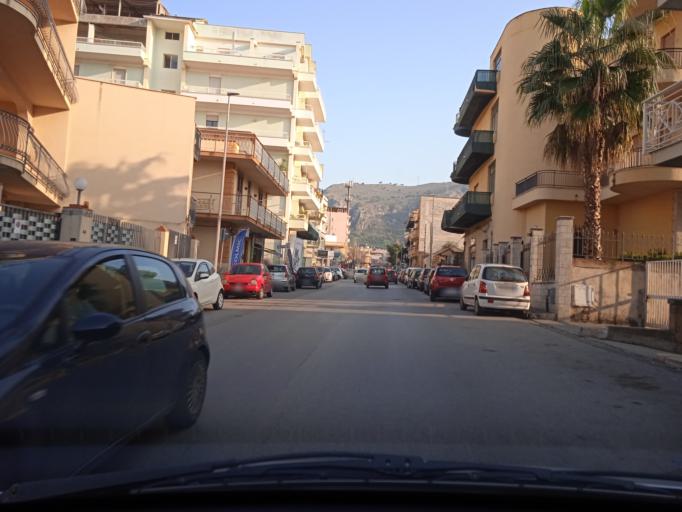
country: IT
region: Sicily
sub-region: Palermo
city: Villabate
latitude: 38.0790
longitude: 13.4373
